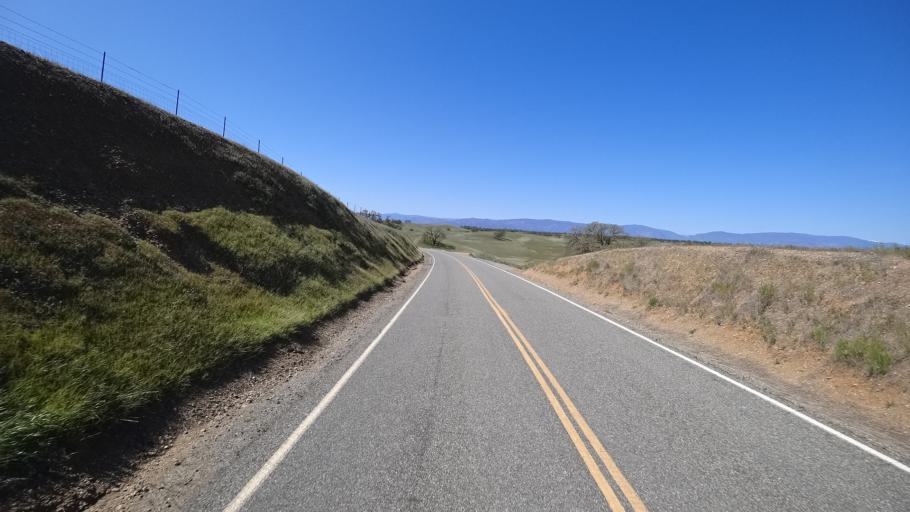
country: US
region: California
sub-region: Tehama County
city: Rancho Tehama Reserve
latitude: 39.8276
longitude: -122.3722
